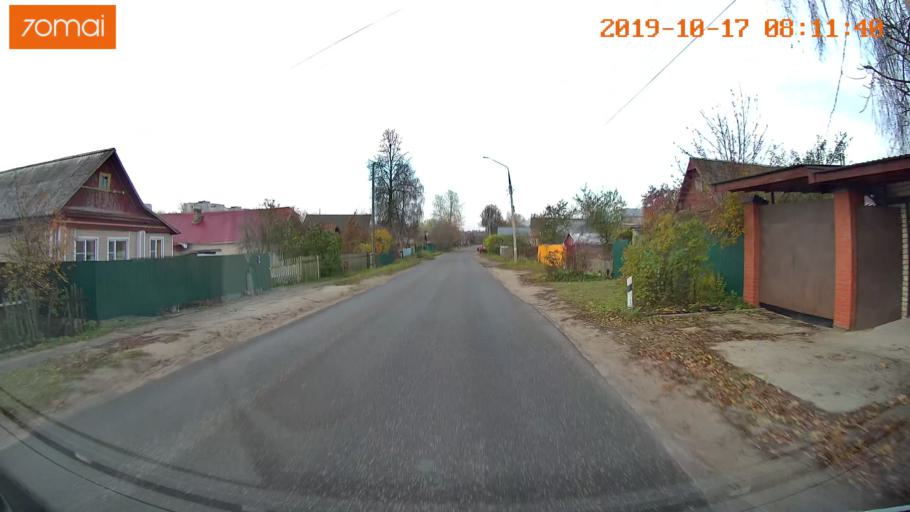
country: RU
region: Vladimir
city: Kol'chugino
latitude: 56.3020
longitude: 39.3666
